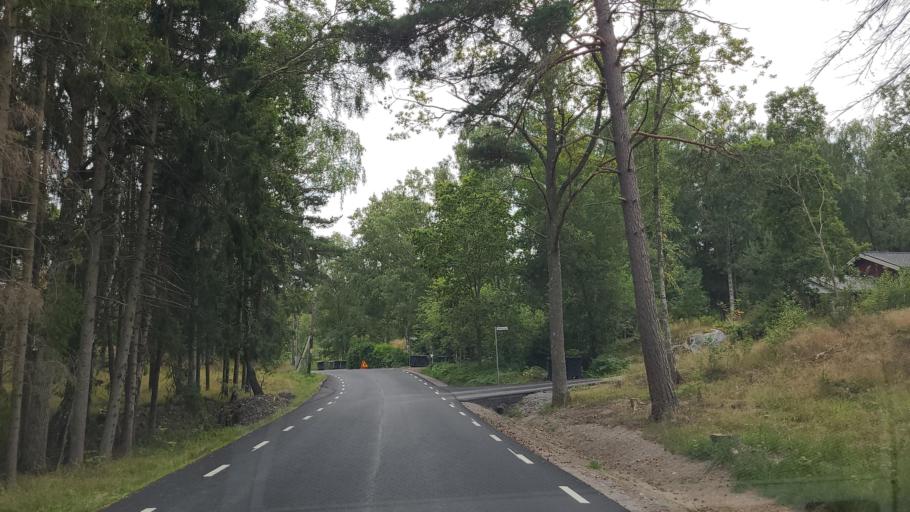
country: SE
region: Stockholm
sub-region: Upplands-Bro Kommun
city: Bro
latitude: 59.4802
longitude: 17.5977
